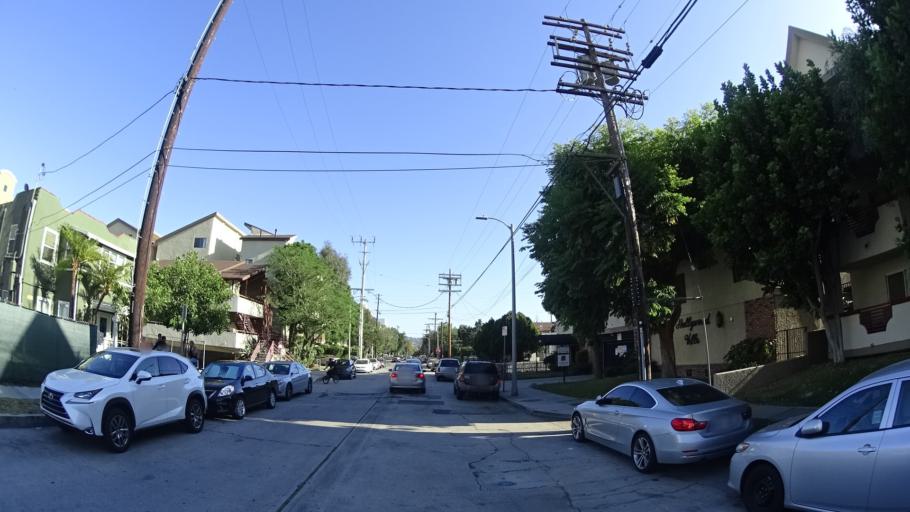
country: US
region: California
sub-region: Los Angeles County
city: North Hollywood
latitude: 34.1639
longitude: -118.3758
